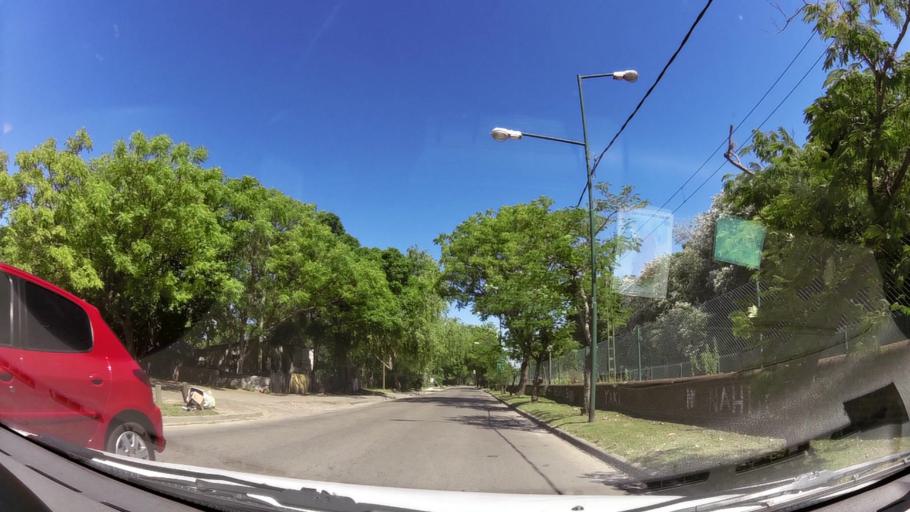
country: AR
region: Buenos Aires
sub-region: Partido de San Isidro
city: San Isidro
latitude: -34.4784
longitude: -58.4842
